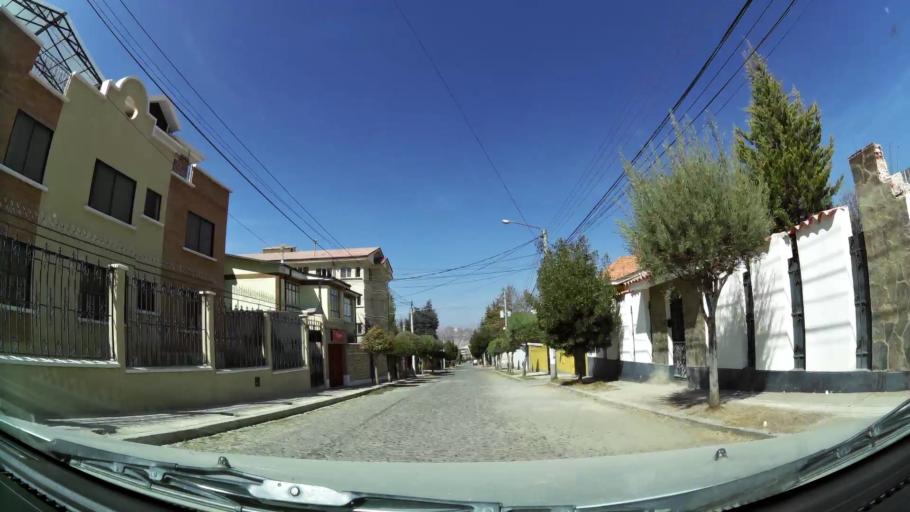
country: BO
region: La Paz
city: La Paz
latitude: -16.5155
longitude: -68.0870
